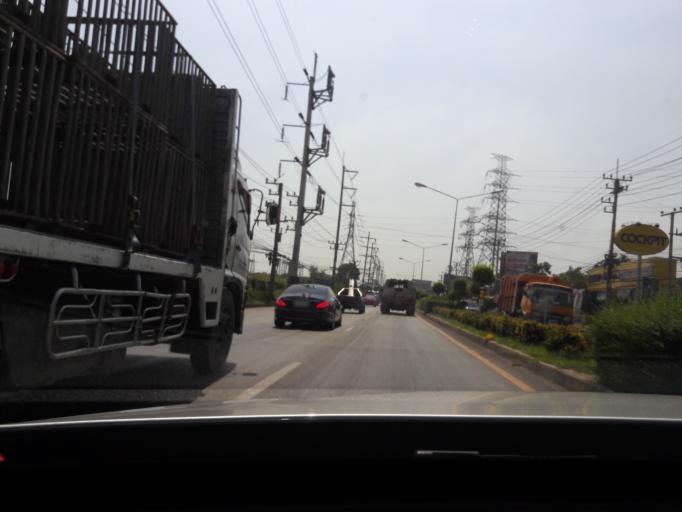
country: TH
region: Samut Sakhon
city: Samut Sakhon
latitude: 13.5954
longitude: 100.2823
